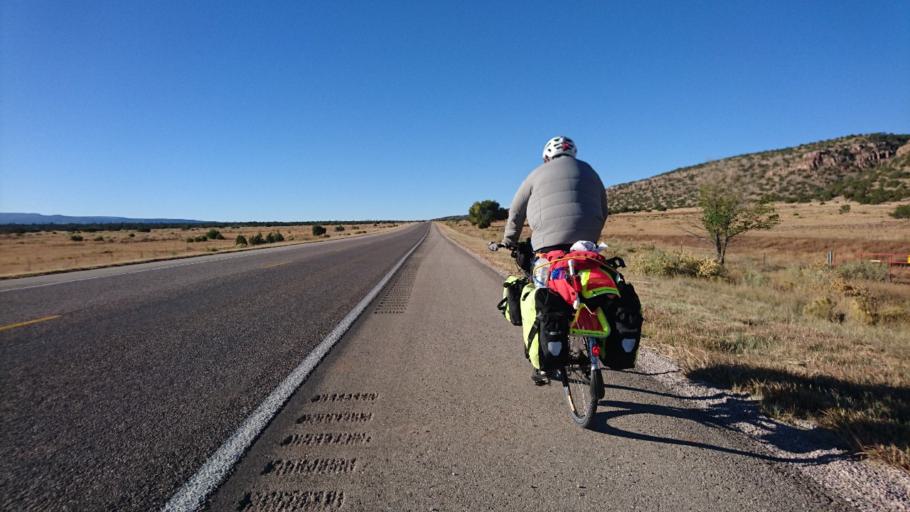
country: US
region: New Mexico
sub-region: Cibola County
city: Grants
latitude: 34.9911
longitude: -107.9006
